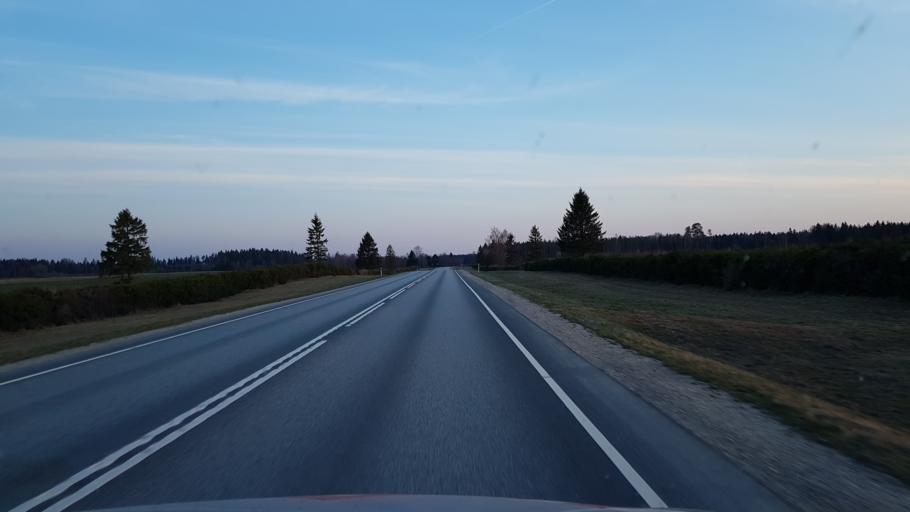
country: EE
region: Laeaene-Virumaa
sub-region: Tapa vald
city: Tapa
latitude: 59.2938
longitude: 26.0520
